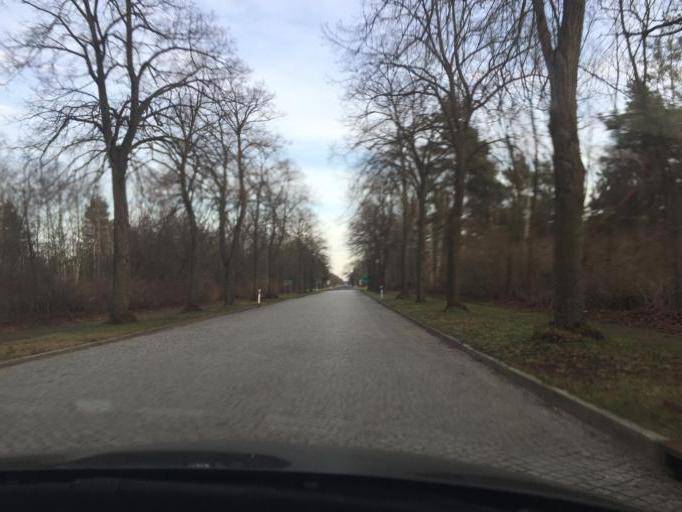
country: DE
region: Brandenburg
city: Forst
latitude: 51.7458
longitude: 14.6734
